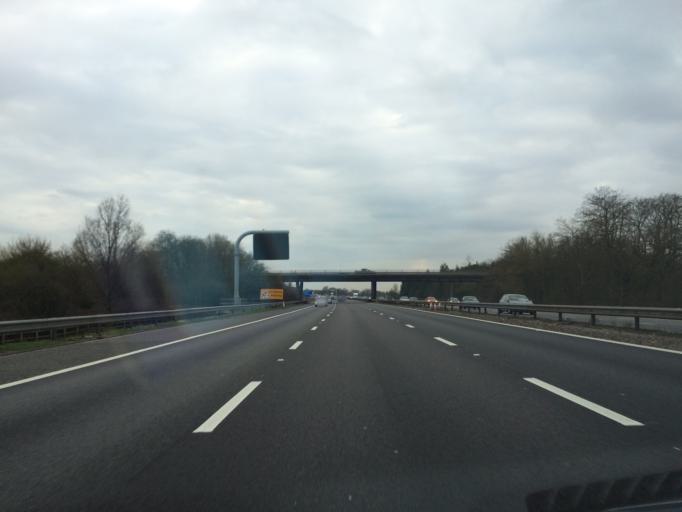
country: GB
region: England
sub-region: Bracknell Forest
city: Binfield
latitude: 51.4472
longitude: -0.8188
